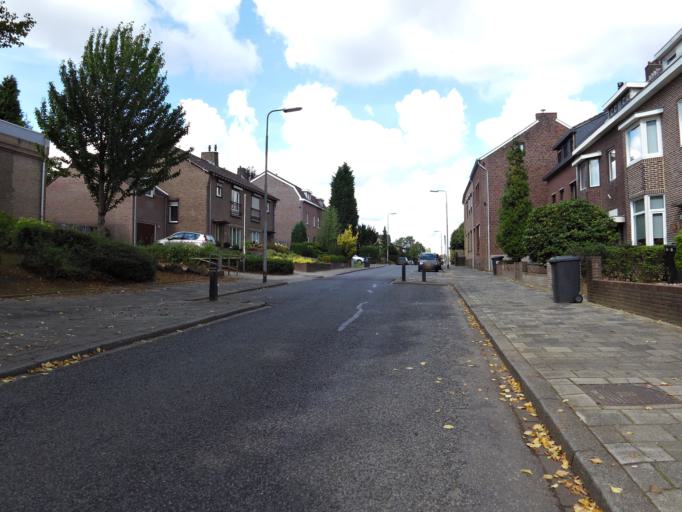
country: NL
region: Limburg
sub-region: Gemeente Kerkrade
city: Kerkrade
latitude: 50.8519
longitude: 6.0281
